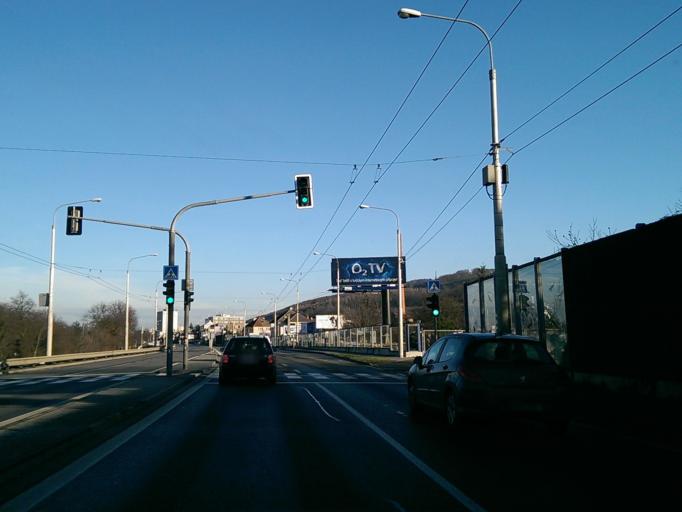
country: CZ
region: Zlin
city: Tecovice
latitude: 49.2102
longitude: 17.6056
